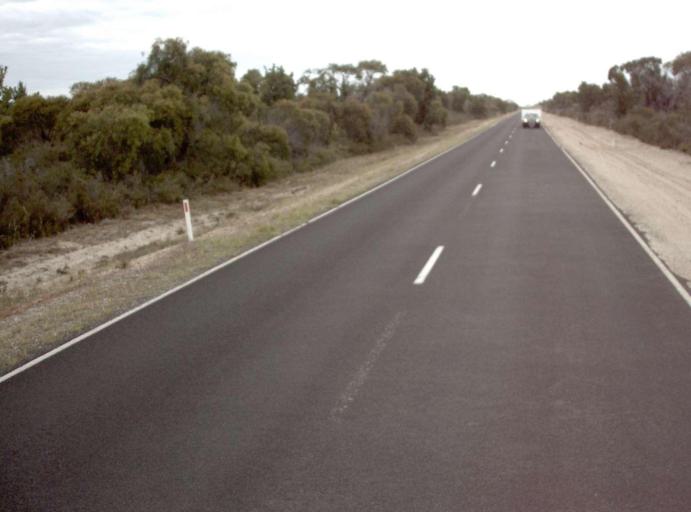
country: AU
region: Victoria
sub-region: East Gippsland
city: Bairnsdale
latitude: -38.1119
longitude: 147.4677
